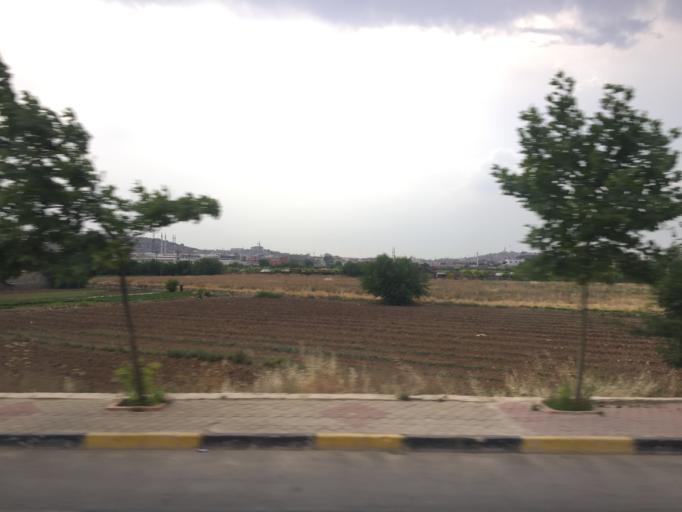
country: TR
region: Gaziantep
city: Gaziantep
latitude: 37.0591
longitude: 37.4157
